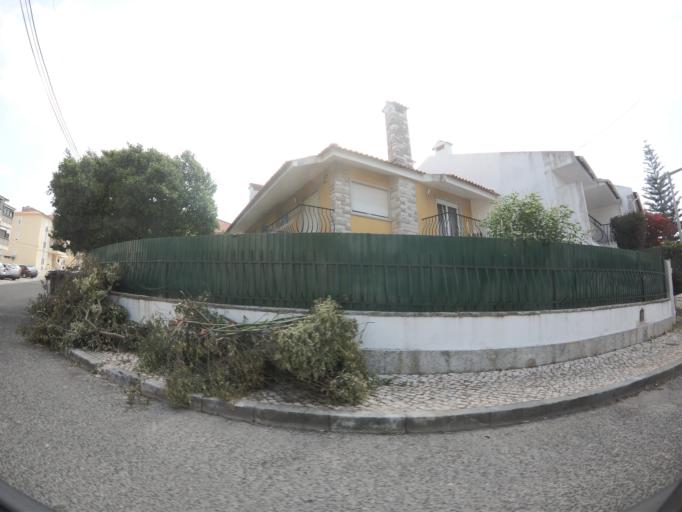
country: PT
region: Lisbon
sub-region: Oeiras
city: Carcavelos
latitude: 38.6910
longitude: -9.3311
